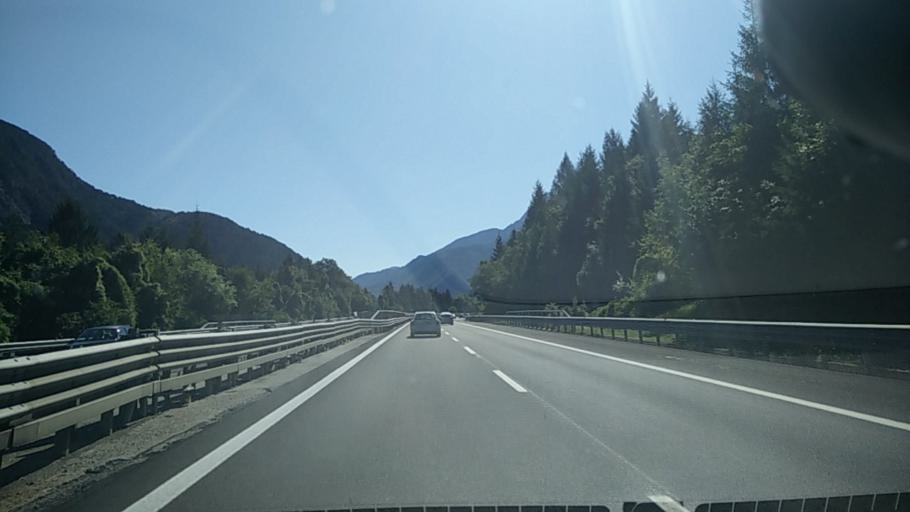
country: IT
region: Friuli Venezia Giulia
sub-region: Provincia di Udine
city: Pontebba
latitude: 46.5064
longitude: 13.3591
